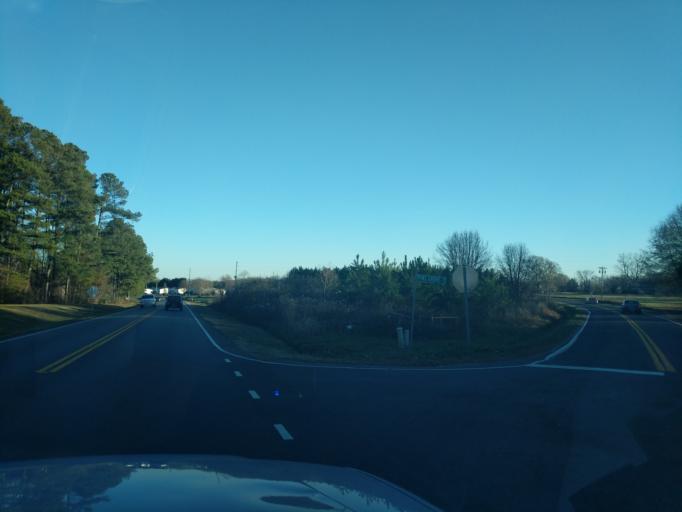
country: US
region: South Carolina
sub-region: Oconee County
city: Seneca
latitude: 34.5950
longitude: -82.9733
